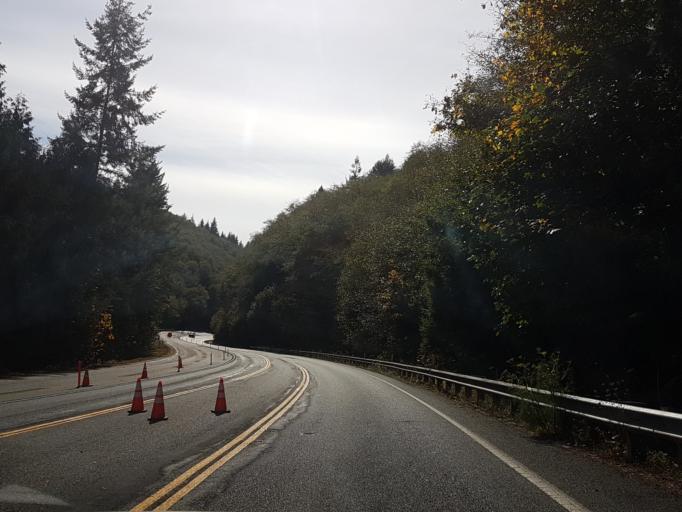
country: US
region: California
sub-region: Del Norte County
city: Bertsch-Oceanview
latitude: 41.4961
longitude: -124.0432
